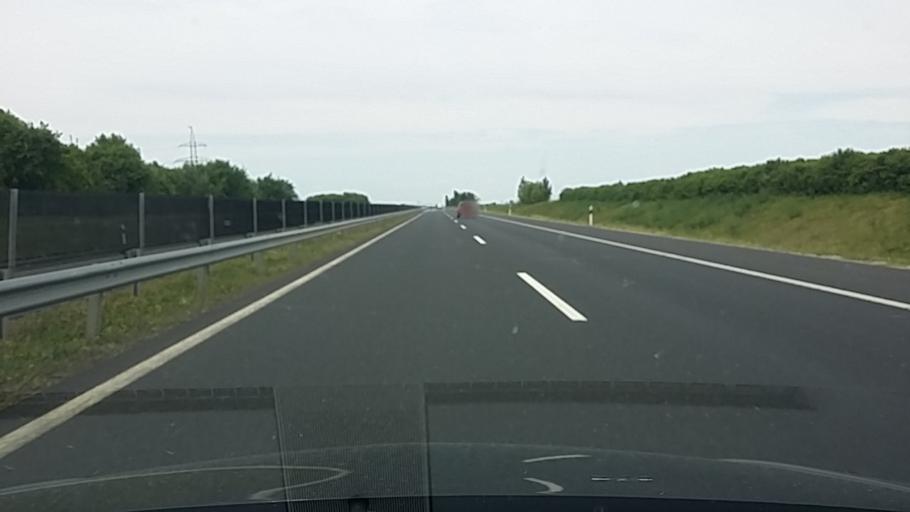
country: HU
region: Fejer
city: Ivancsa
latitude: 47.1889
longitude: 18.8127
